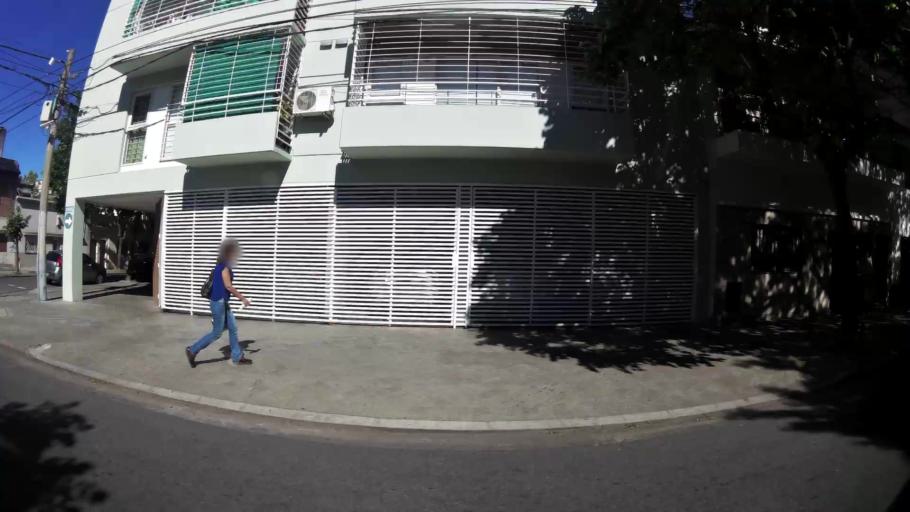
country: AR
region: Santa Fe
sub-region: Departamento de Rosario
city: Rosario
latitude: -32.9464
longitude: -60.6740
